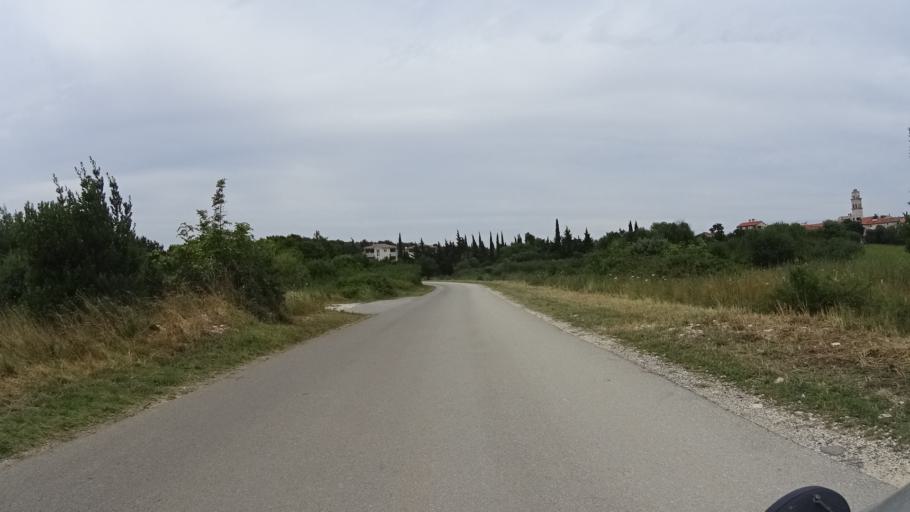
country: HR
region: Istarska
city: Medulin
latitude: 44.7998
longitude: 13.9059
